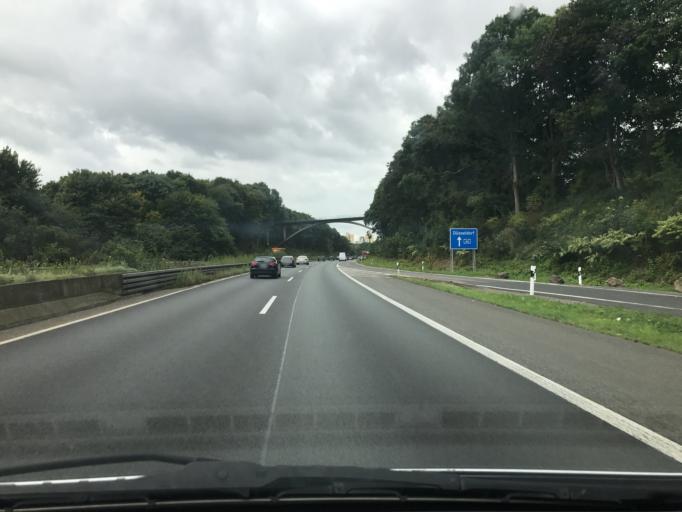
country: DE
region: North Rhine-Westphalia
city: Sprockhovel
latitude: 51.3061
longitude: 7.2339
